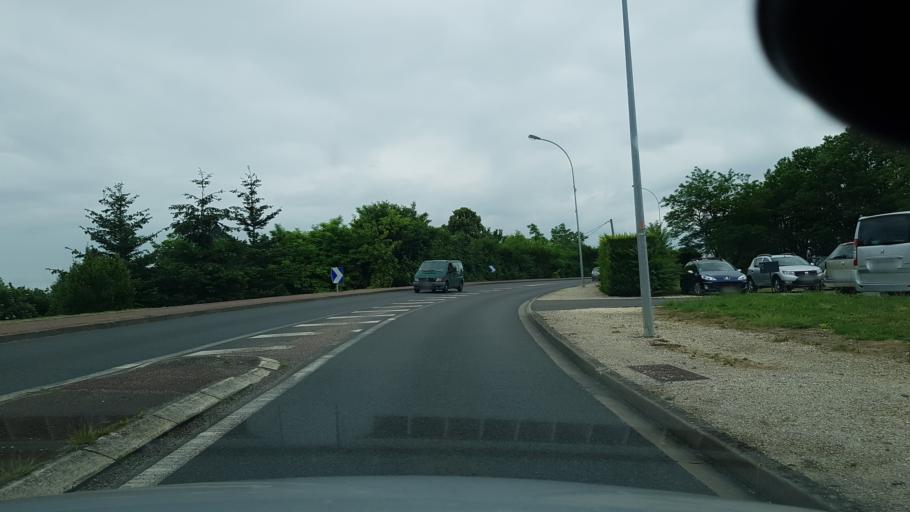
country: FR
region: Centre
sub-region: Departement du Loir-et-Cher
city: Selles-sur-Cher
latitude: 47.2833
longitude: 1.5420
